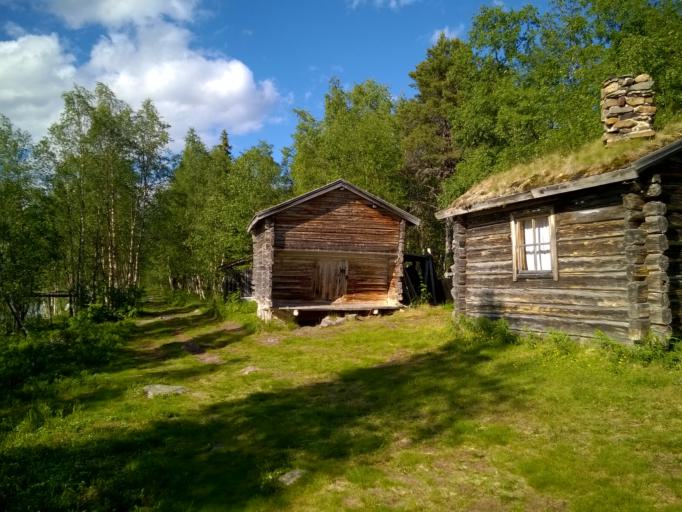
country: FI
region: Lapland
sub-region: Tunturi-Lappi
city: Muonio
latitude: 67.9265
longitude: 24.0462
